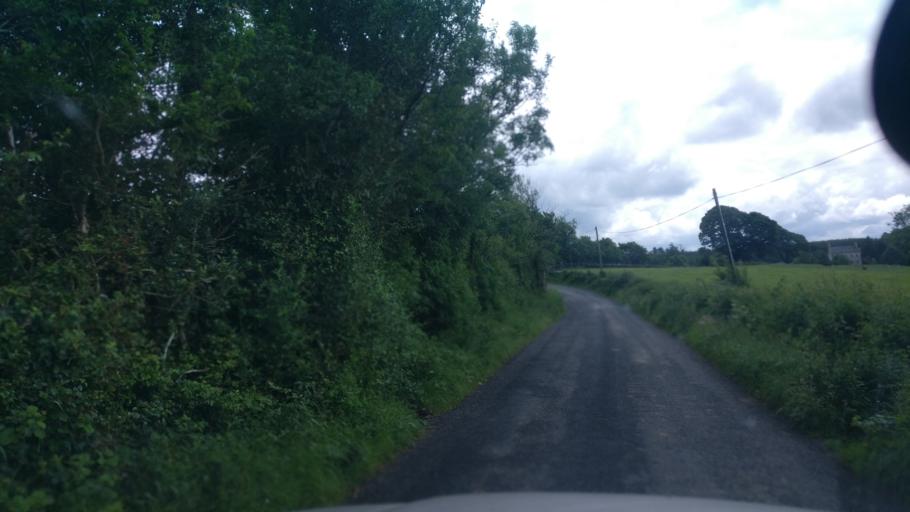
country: IE
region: Connaught
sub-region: County Galway
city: Loughrea
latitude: 53.1591
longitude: -8.5718
